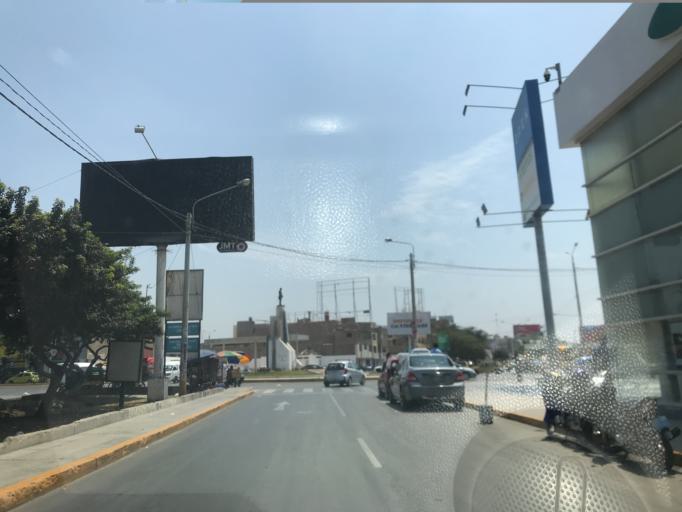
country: PE
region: Lambayeque
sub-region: Provincia de Chiclayo
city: Chiclayo
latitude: -6.7773
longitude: -79.8361
